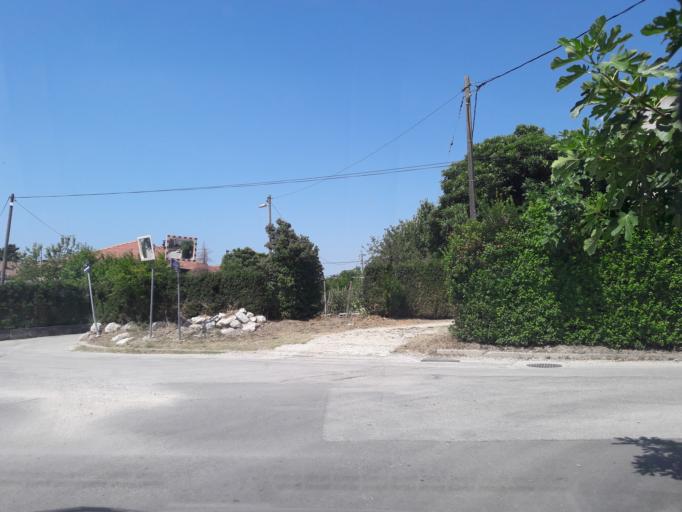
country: HR
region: Splitsko-Dalmatinska
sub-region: Grad Split
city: Split
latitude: 43.5502
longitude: 16.4005
